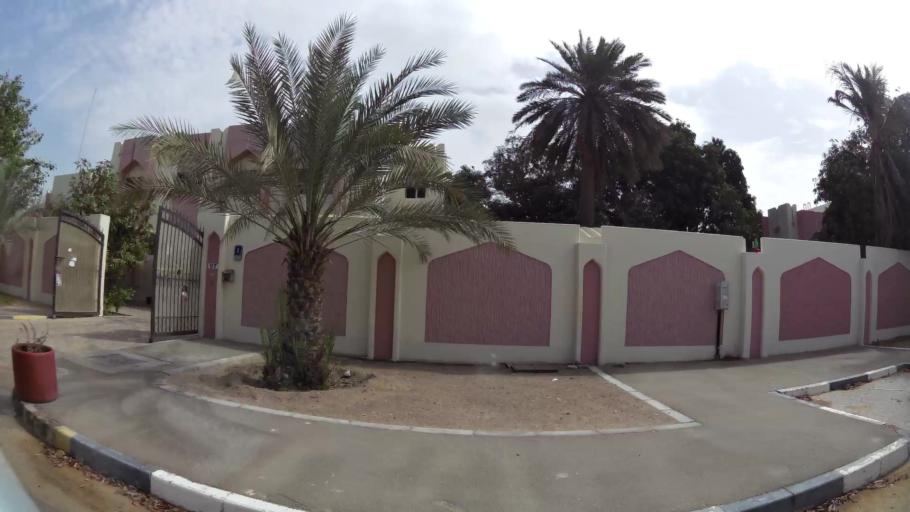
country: AE
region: Abu Dhabi
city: Abu Dhabi
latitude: 24.3936
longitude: 54.5075
